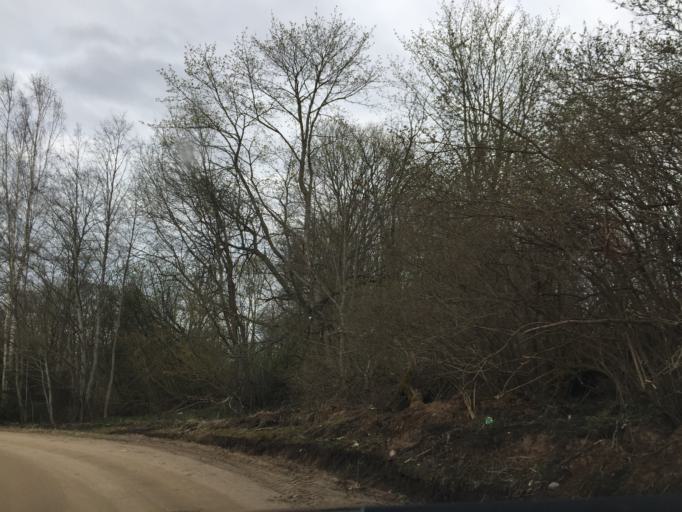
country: LV
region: Aluksnes Rajons
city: Aluksne
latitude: 57.4167
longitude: 27.0330
